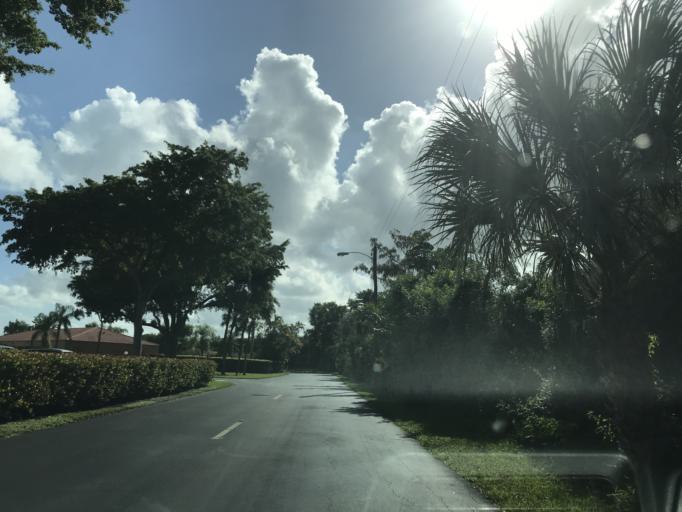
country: US
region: Florida
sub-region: Broward County
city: Margate
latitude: 26.2612
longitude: -80.1976
